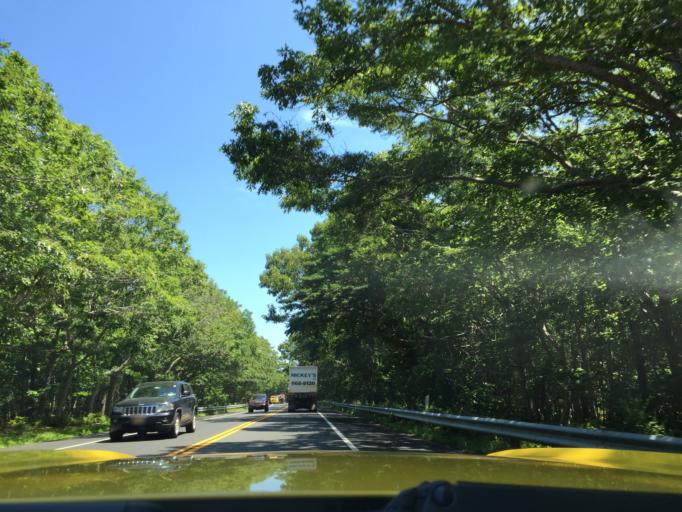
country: US
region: New York
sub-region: Suffolk County
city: Montauk
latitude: 41.0243
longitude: -71.9876
